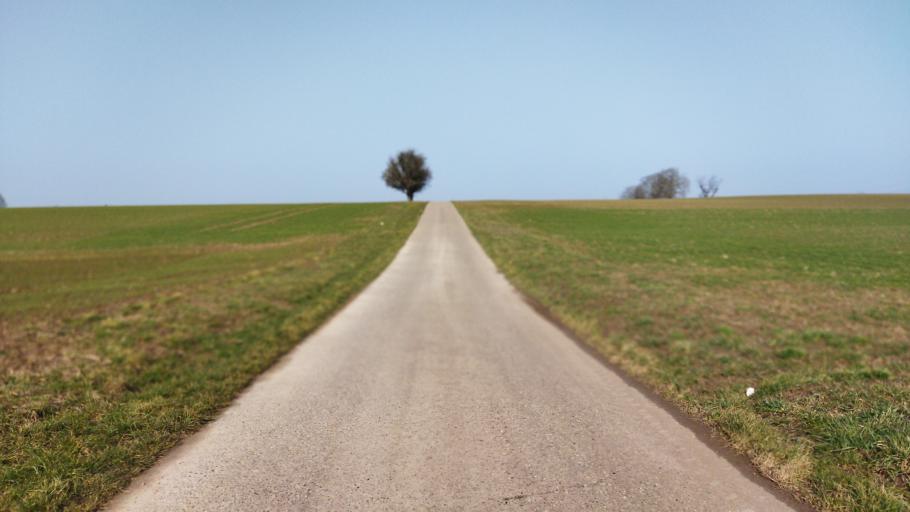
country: DE
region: Baden-Wuerttemberg
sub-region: Regierungsbezirk Stuttgart
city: Nordheim
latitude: 49.1293
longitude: 9.1624
